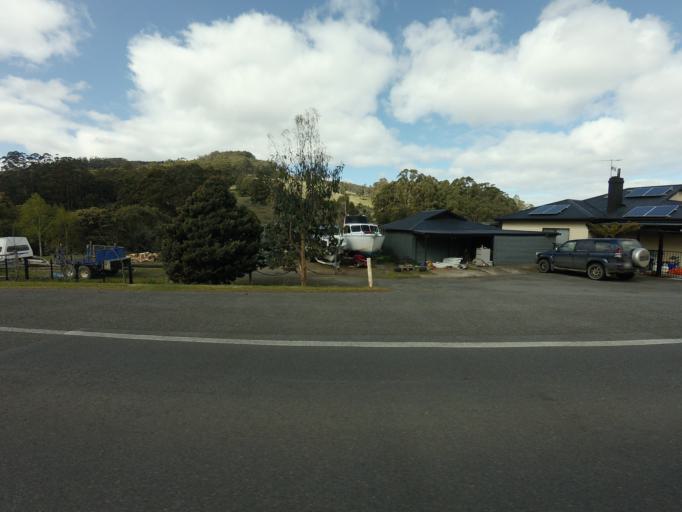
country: AU
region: Tasmania
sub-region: Huon Valley
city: Geeveston
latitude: -43.3013
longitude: 147.0074
